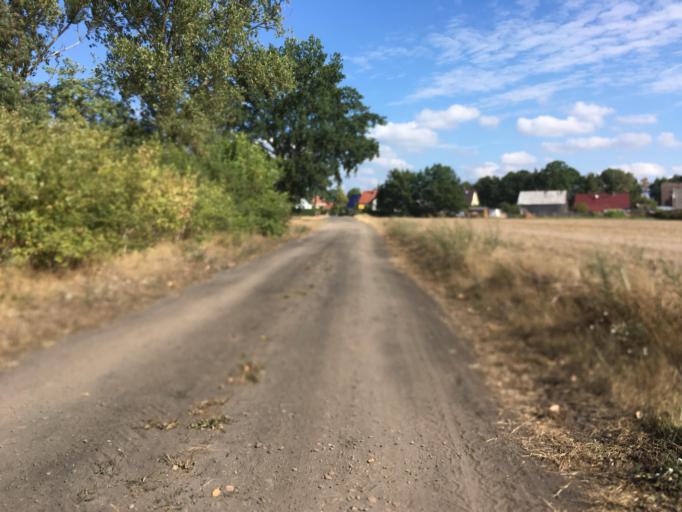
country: DE
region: Brandenburg
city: Zehdenick
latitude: 52.9803
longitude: 13.3804
